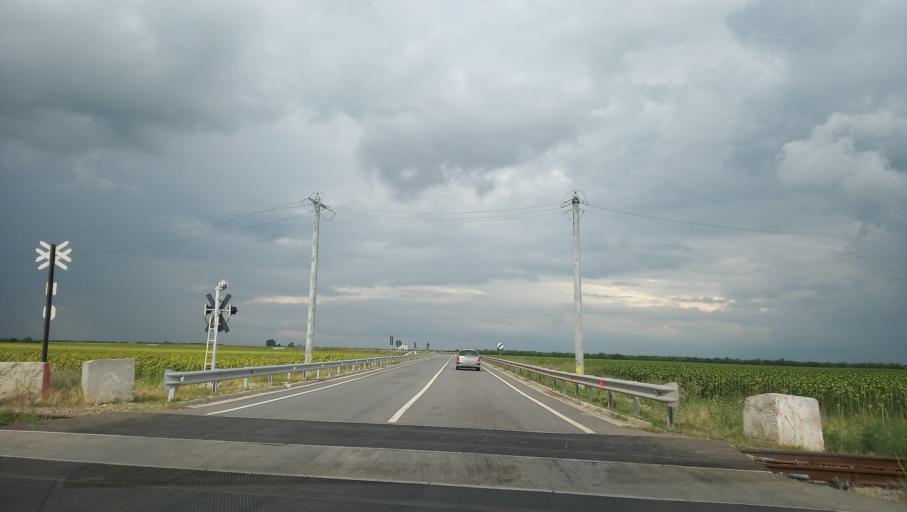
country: RO
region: Olt
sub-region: Comuna Deveselu
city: Comanca
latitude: 44.0943
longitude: 24.3768
